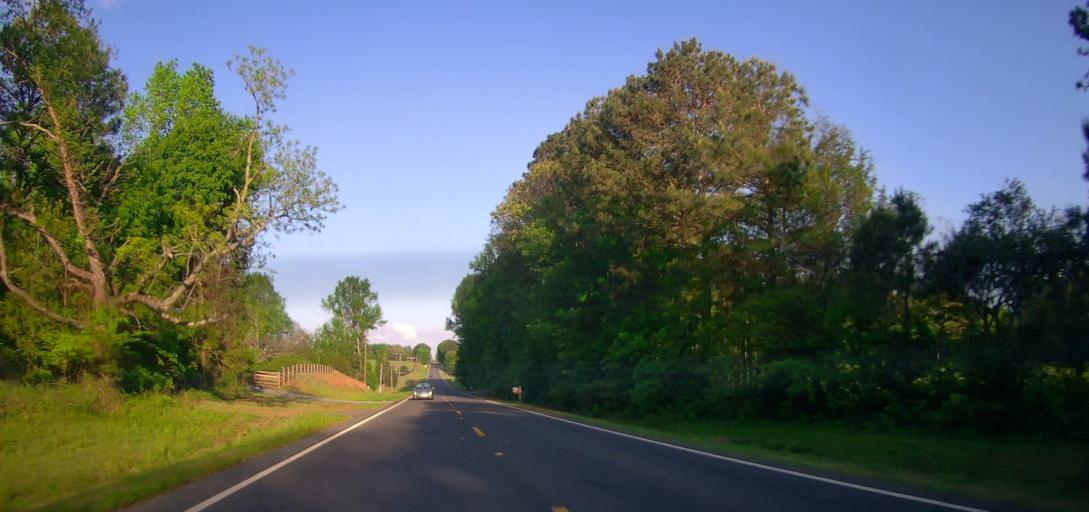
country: US
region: Georgia
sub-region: Walton County
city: Social Circle
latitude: 33.5071
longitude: -83.6648
